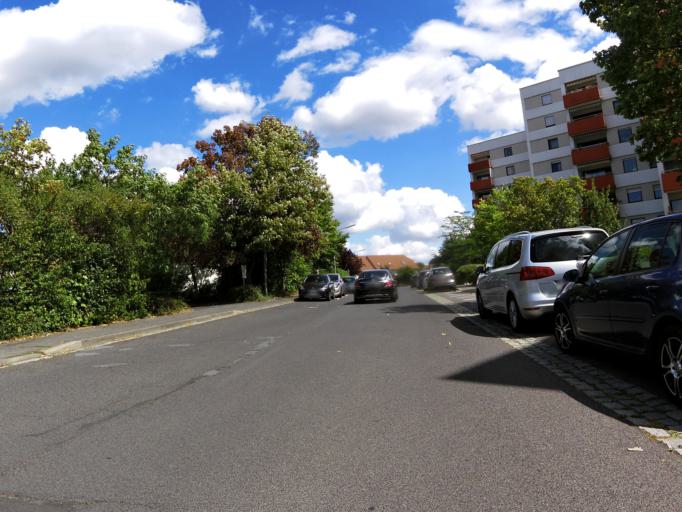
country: DE
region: Bavaria
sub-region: Regierungsbezirk Unterfranken
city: Hochberg
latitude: 49.7906
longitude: 9.8841
